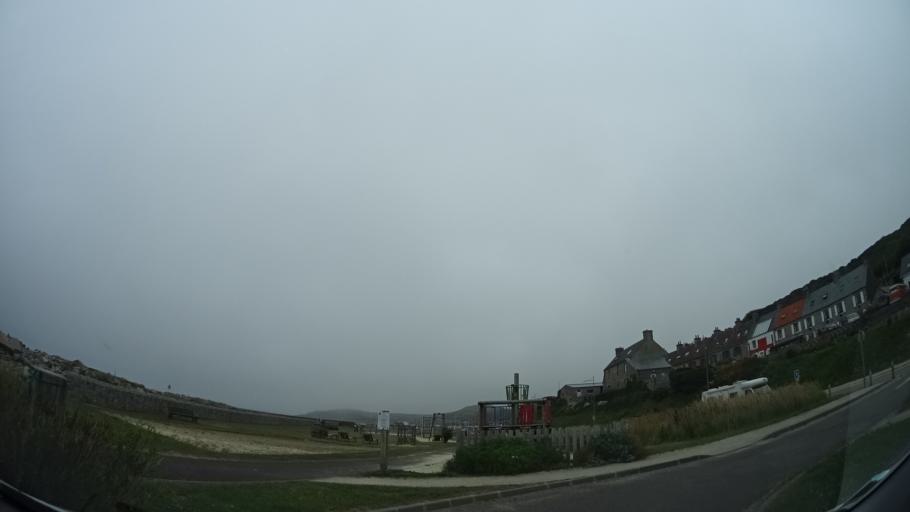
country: FR
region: Lower Normandy
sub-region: Departement de la Manche
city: Flamanville
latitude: 49.5495
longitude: -1.8653
